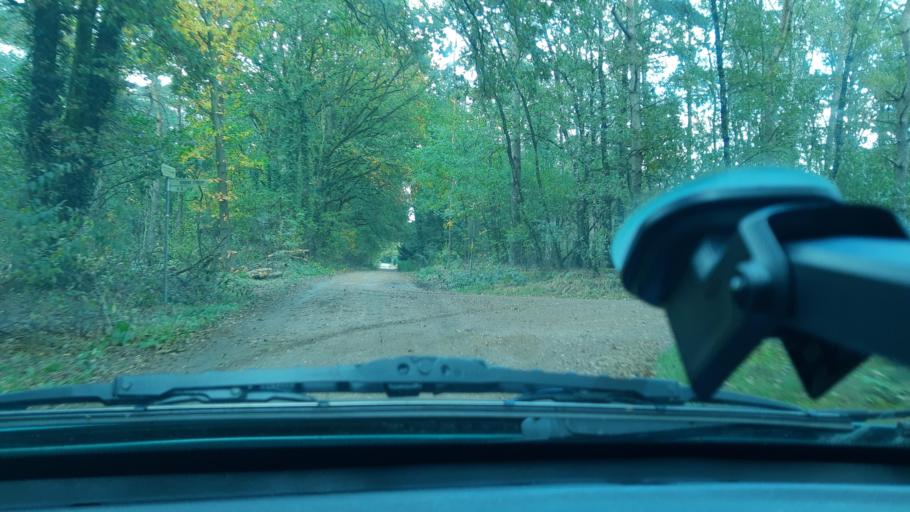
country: NL
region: Limburg
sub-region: Gemeente Gennep
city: Gennep
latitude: 51.6545
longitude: 6.0107
